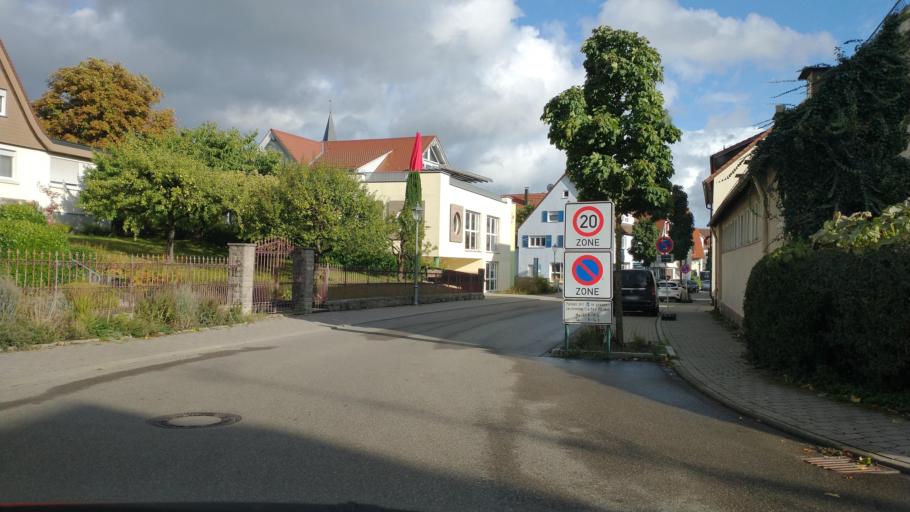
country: DE
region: Baden-Wuerttemberg
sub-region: Regierungsbezirk Stuttgart
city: Welzheim
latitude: 48.8753
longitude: 9.6319
